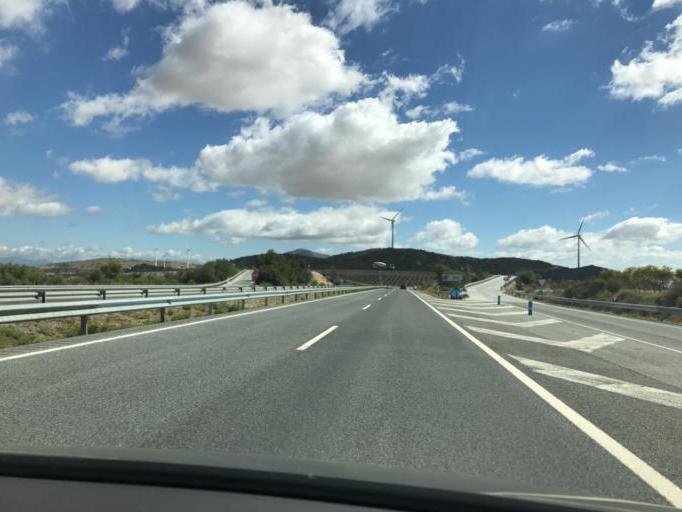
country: ES
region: Andalusia
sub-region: Provincia de Granada
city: Zujar
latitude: 37.4844
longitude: -2.8504
